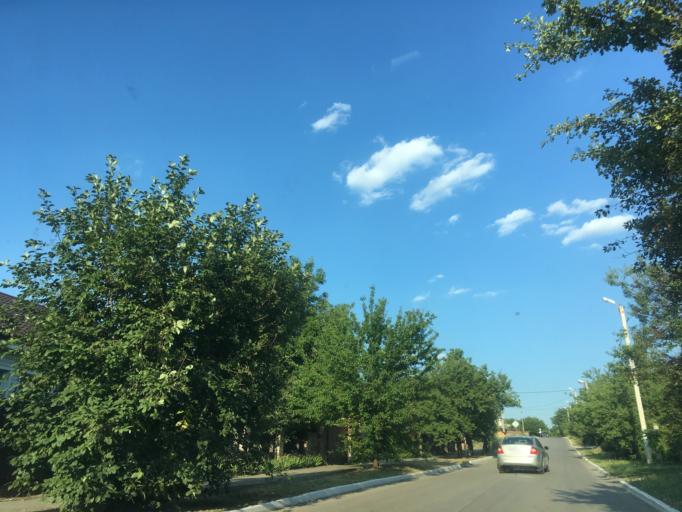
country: RU
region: Rostov
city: Masalovka
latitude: 48.4006
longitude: 40.2775
